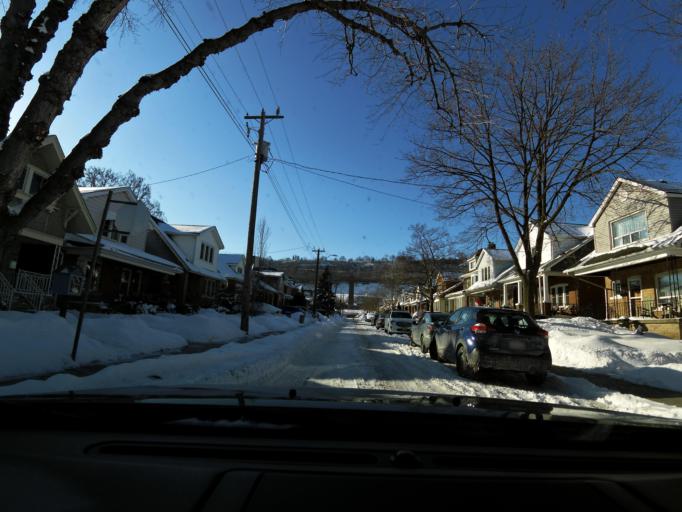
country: CA
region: Ontario
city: Hamilton
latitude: 43.2378
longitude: -79.8252
